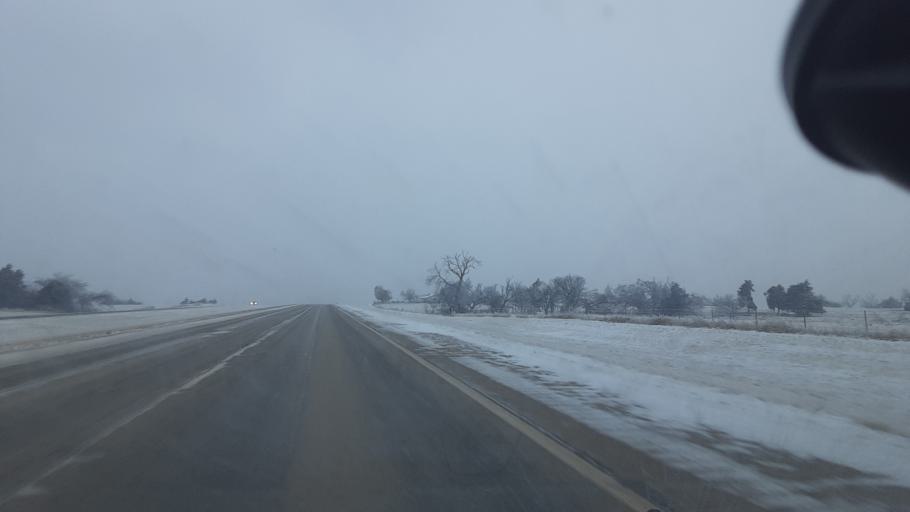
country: US
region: Oklahoma
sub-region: Logan County
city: Guthrie
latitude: 35.9014
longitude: -97.3480
